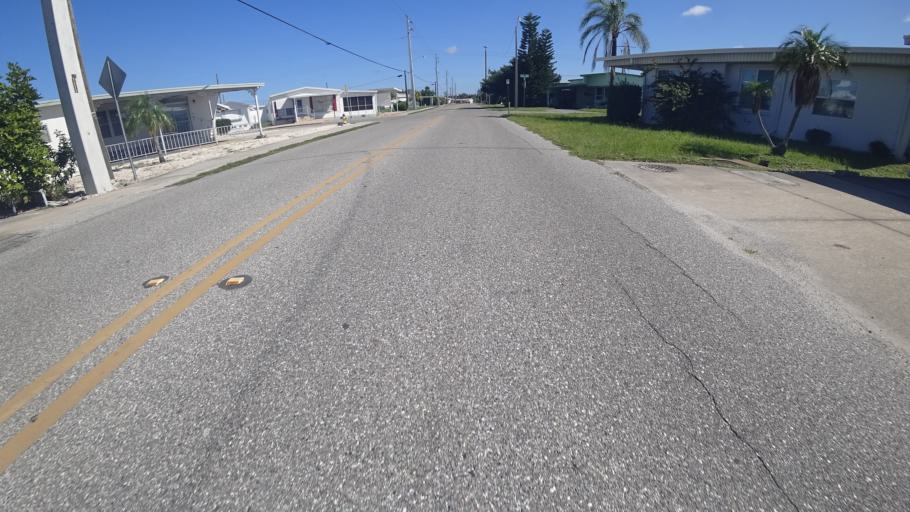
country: US
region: Florida
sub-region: Manatee County
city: Bayshore Gardens
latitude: 27.4202
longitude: -82.5806
